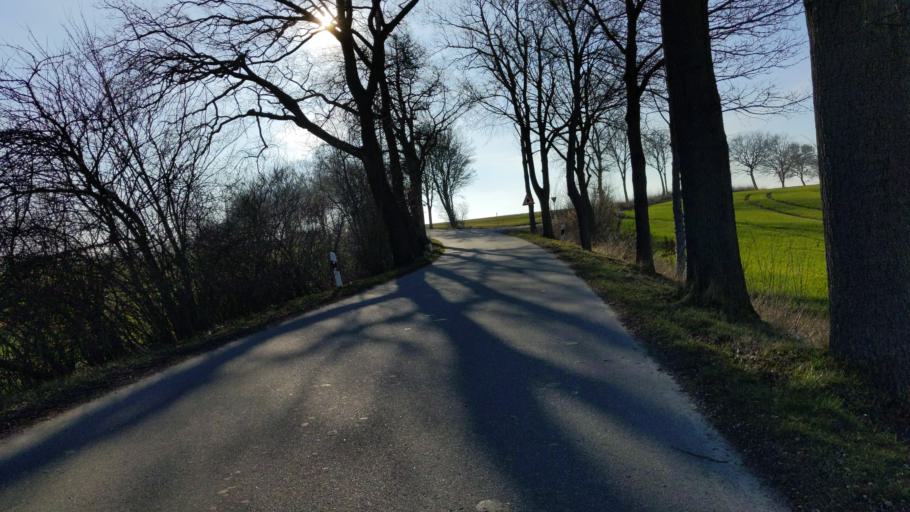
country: DE
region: Schleswig-Holstein
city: Susel
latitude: 54.0241
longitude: 10.6570
